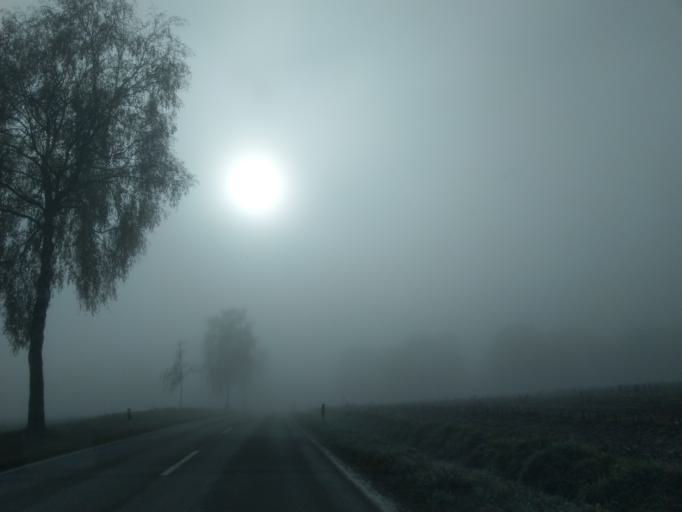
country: DE
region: Bavaria
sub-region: Lower Bavaria
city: Aussernzell
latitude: 48.7381
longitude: 13.1998
